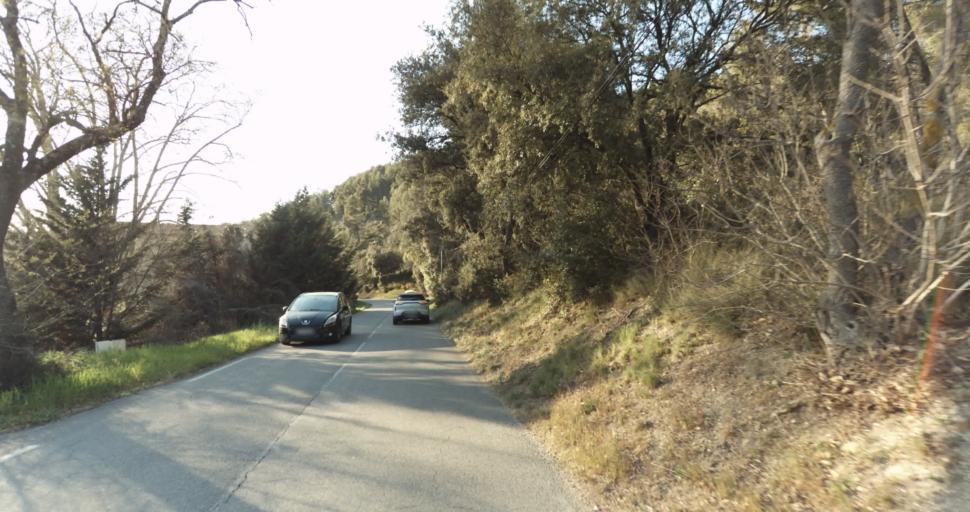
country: FR
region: Provence-Alpes-Cote d'Azur
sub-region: Departement des Bouches-du-Rhone
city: Ventabren
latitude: 43.5185
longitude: 5.3029
